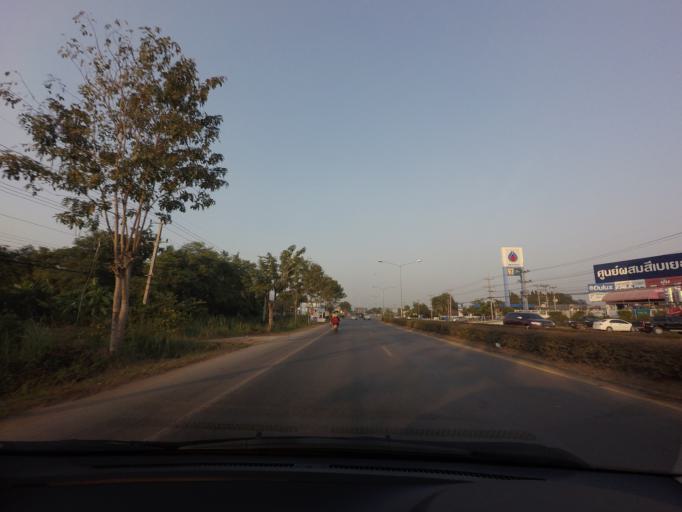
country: TH
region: Sukhothai
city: Sukhothai
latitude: 17.0187
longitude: 99.8119
